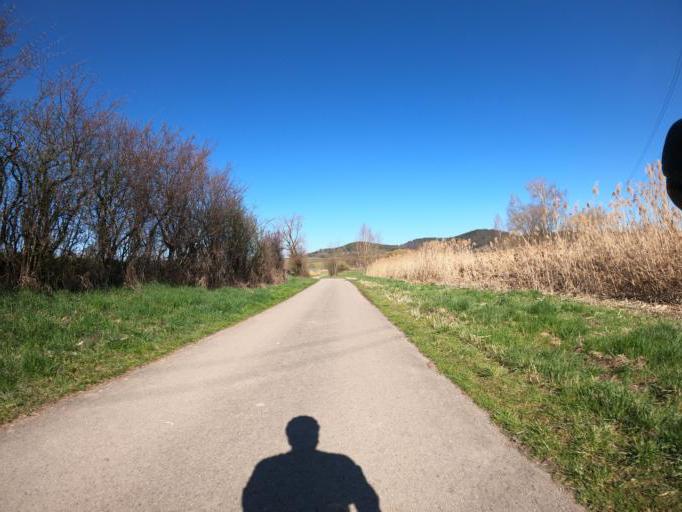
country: DE
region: Baden-Wuerttemberg
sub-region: Tuebingen Region
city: Rangendingen
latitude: 48.3850
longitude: 8.8747
